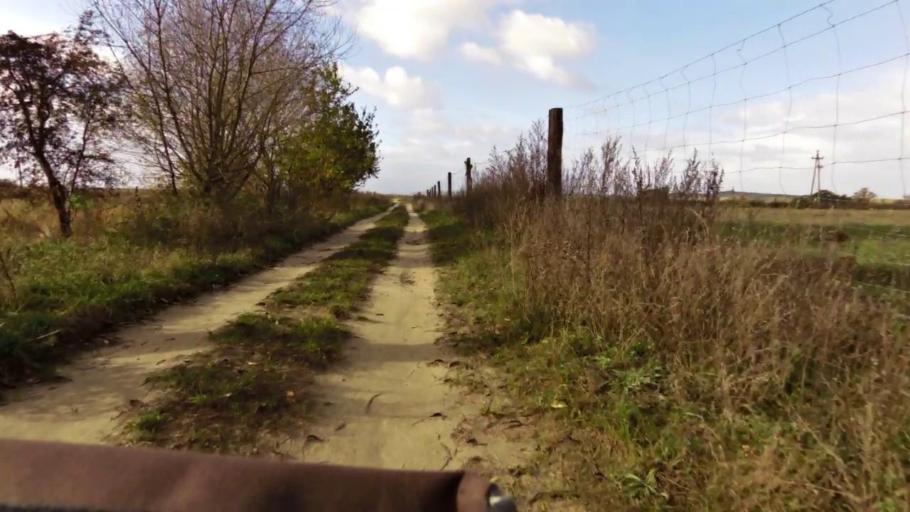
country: PL
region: West Pomeranian Voivodeship
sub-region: Powiat kamienski
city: Wolin
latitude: 53.8398
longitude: 14.6064
